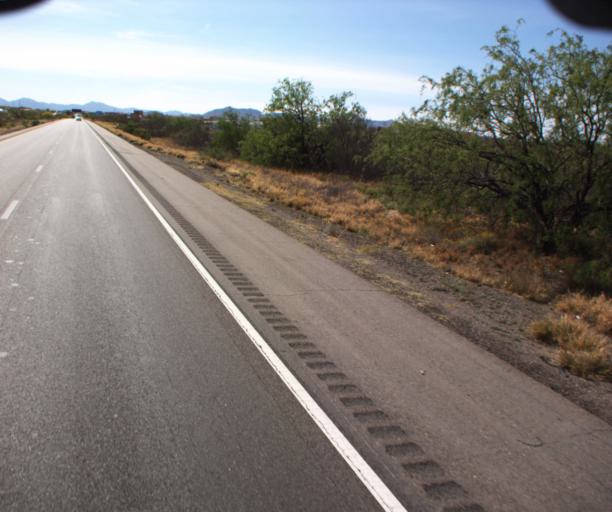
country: US
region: Arizona
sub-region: Pima County
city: Vail
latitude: 32.0182
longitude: -110.7074
